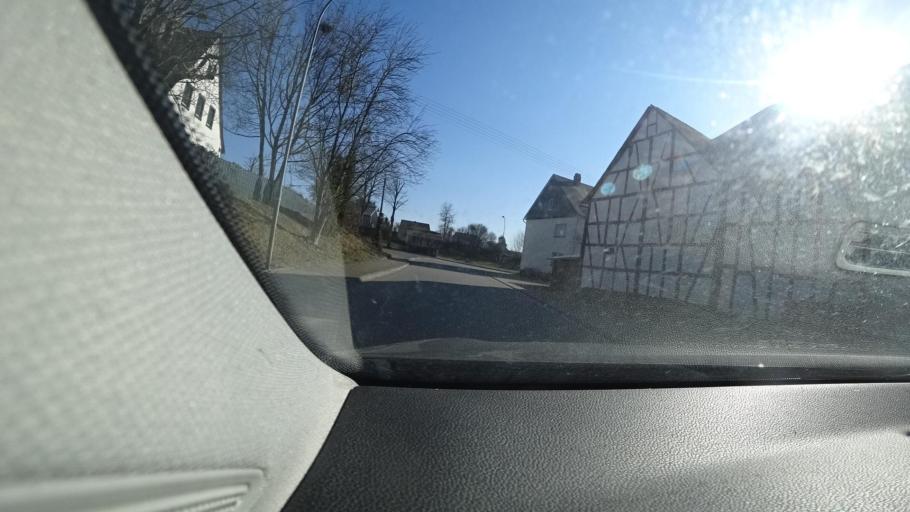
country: DE
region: Rheinland-Pfalz
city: Morschbach
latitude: 50.0119
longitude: 7.6257
